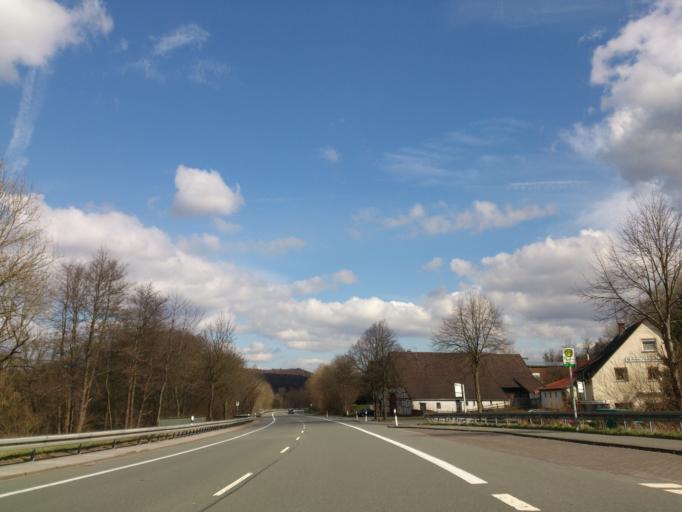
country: DE
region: North Rhine-Westphalia
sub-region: Regierungsbezirk Detmold
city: Bad Driburg
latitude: 51.7231
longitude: 9.0443
